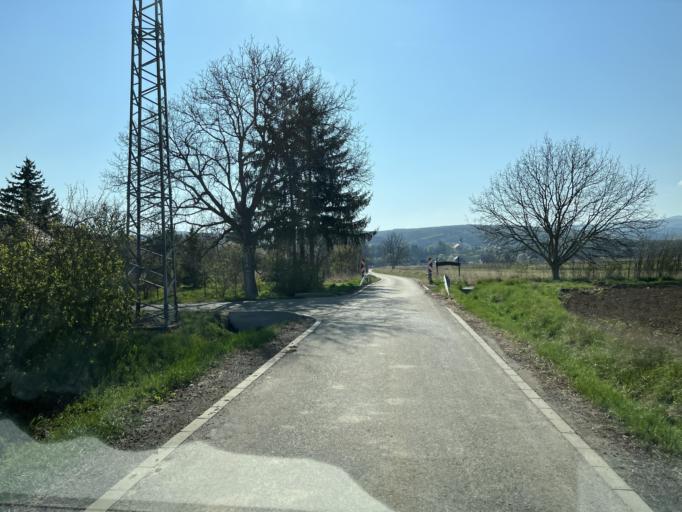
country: SK
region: Nitriansky
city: Sahy
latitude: 48.0416
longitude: 18.9052
